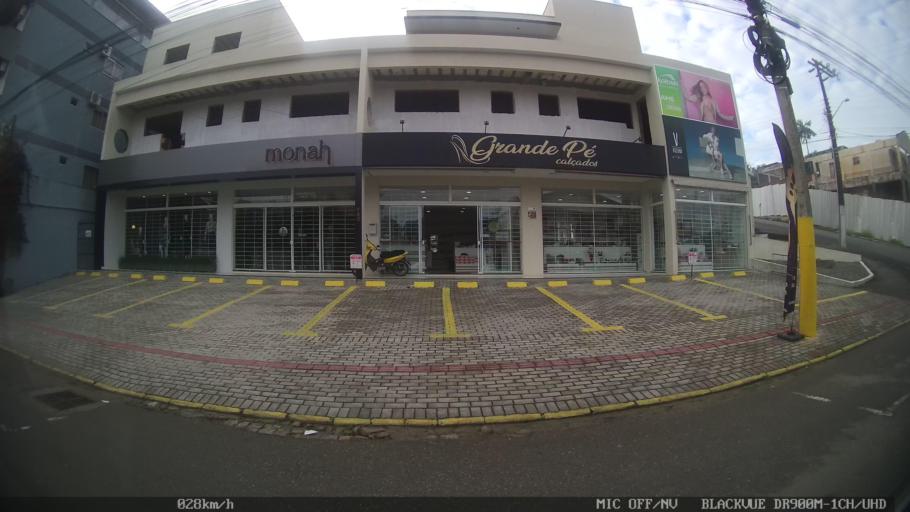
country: BR
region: Santa Catarina
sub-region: Barra Velha
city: Barra Velha
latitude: -26.6340
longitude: -48.6849
